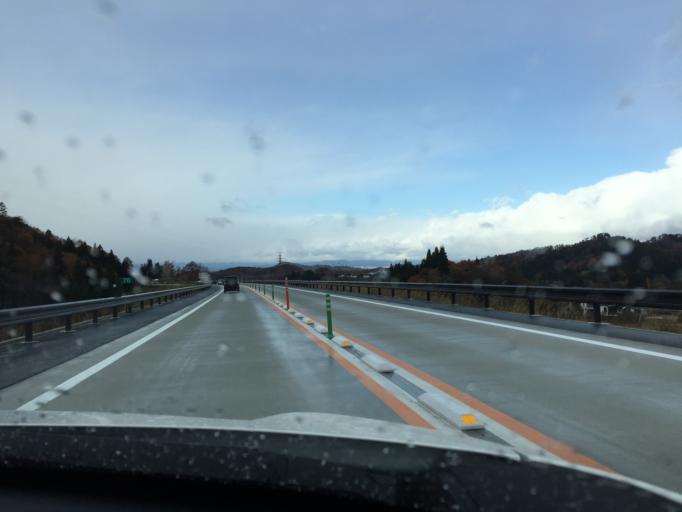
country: JP
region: Yamagata
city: Yonezawa
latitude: 37.8871
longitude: 140.1723
